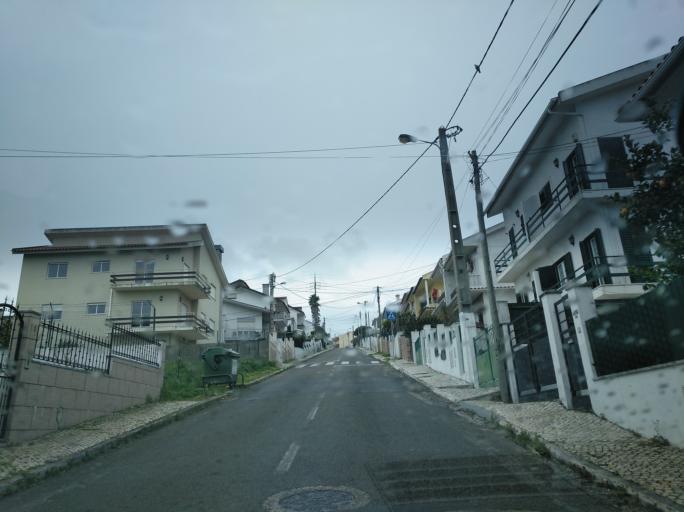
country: PT
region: Lisbon
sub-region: Odivelas
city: Famoes
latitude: 38.7945
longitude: -9.2119
